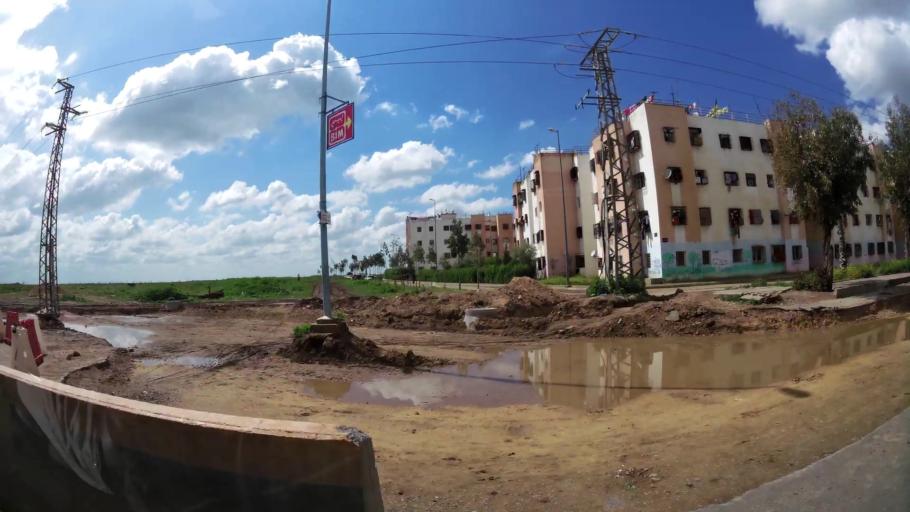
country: MA
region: Chaouia-Ouardigha
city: Nouaseur
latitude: 33.3621
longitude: -7.5461
